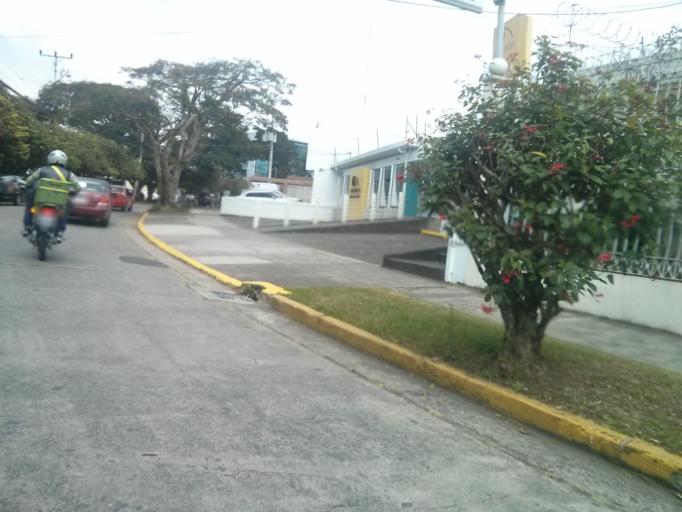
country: CR
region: San Jose
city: San Pedro
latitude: 9.9331
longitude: -84.0600
